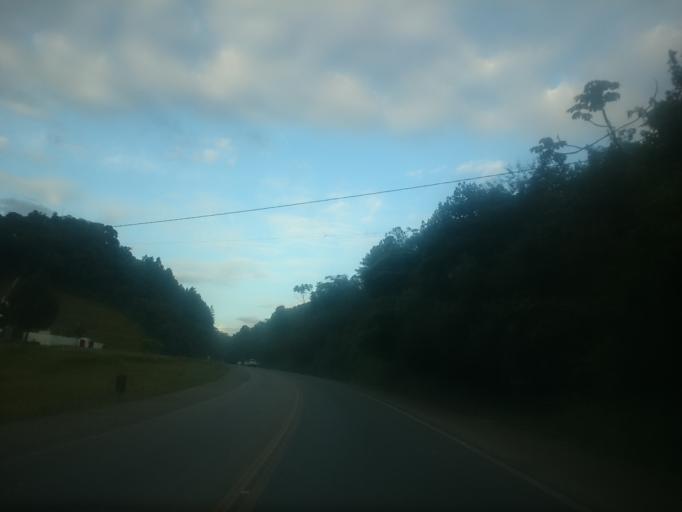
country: BR
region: Santa Catarina
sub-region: Blumenau
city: Blumenau
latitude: -26.8639
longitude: -49.0452
